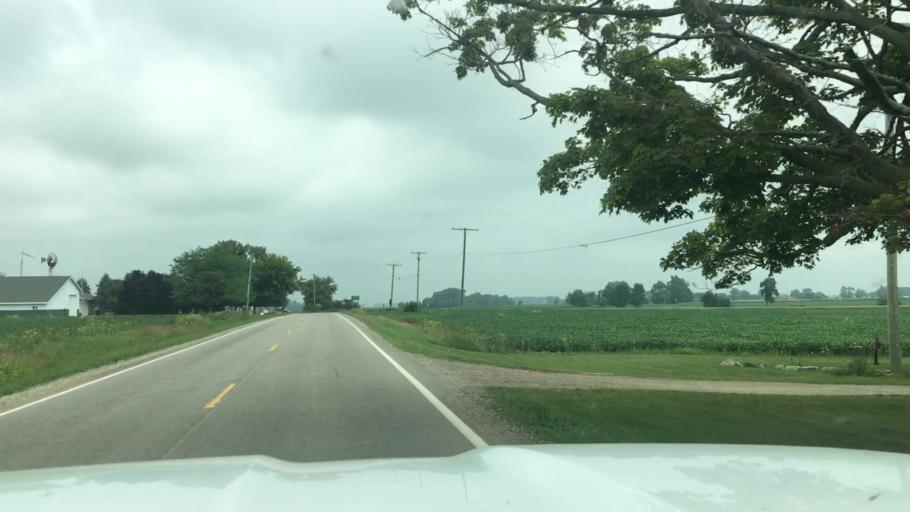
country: US
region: Michigan
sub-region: Sanilac County
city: Marlette
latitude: 43.3277
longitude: -82.9843
